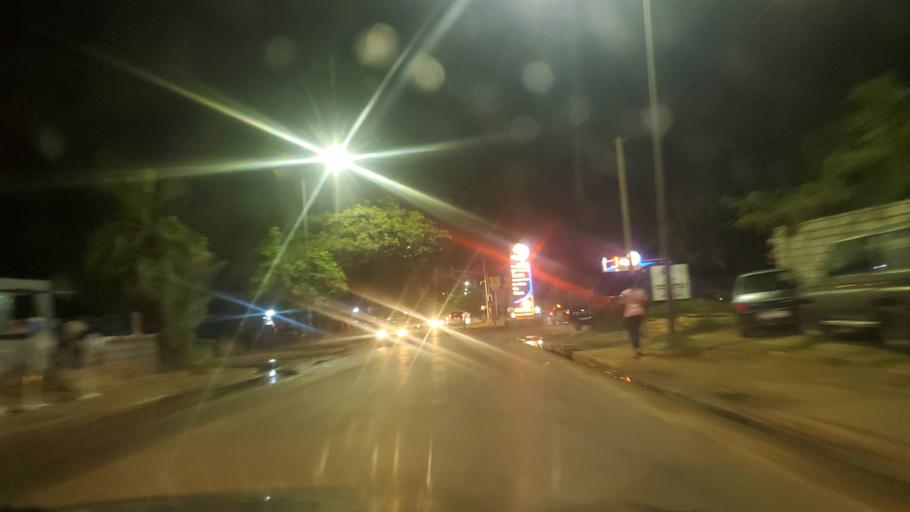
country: SN
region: Dakar
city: Mermoz Boabab
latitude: 14.7033
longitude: -17.4636
